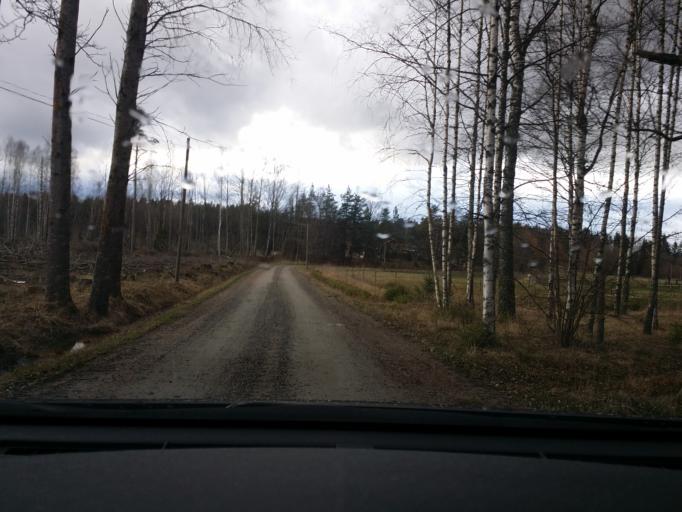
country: SE
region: Soedermanland
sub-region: Eskilstuna Kommun
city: Arla
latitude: 59.3715
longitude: 16.6652
